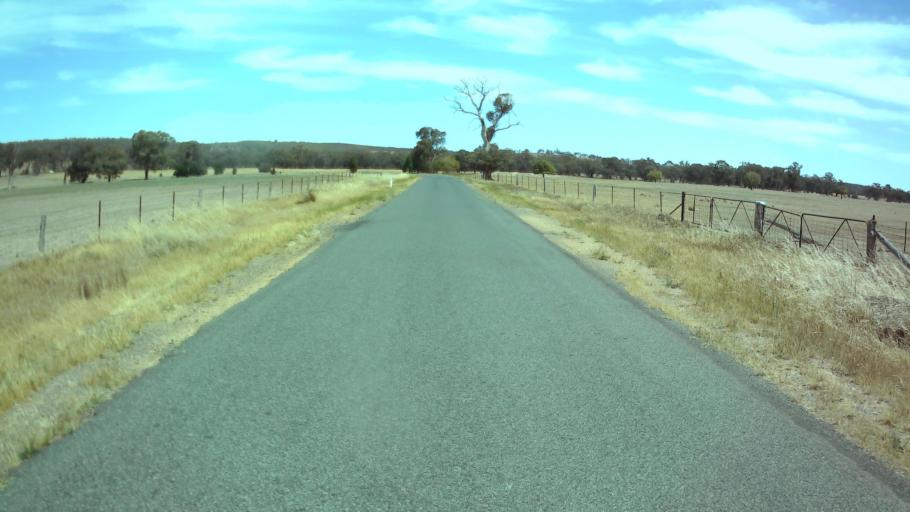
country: AU
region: New South Wales
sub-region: Weddin
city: Grenfell
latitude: -33.8409
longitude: 148.1772
